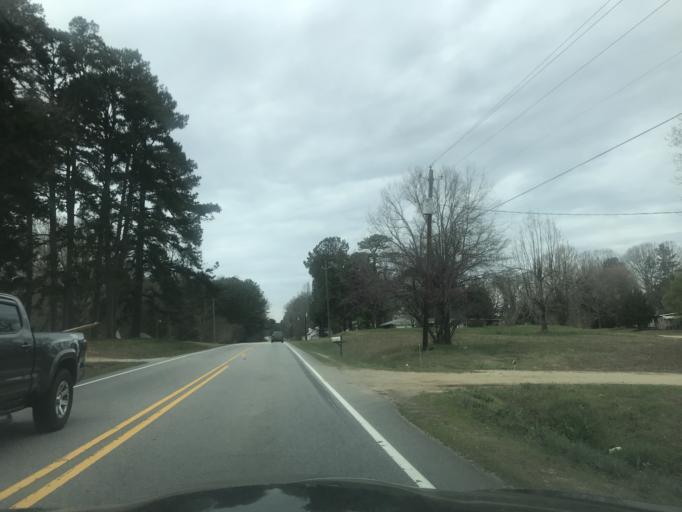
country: US
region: North Carolina
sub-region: Franklin County
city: Franklinton
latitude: 36.1095
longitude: -78.4757
